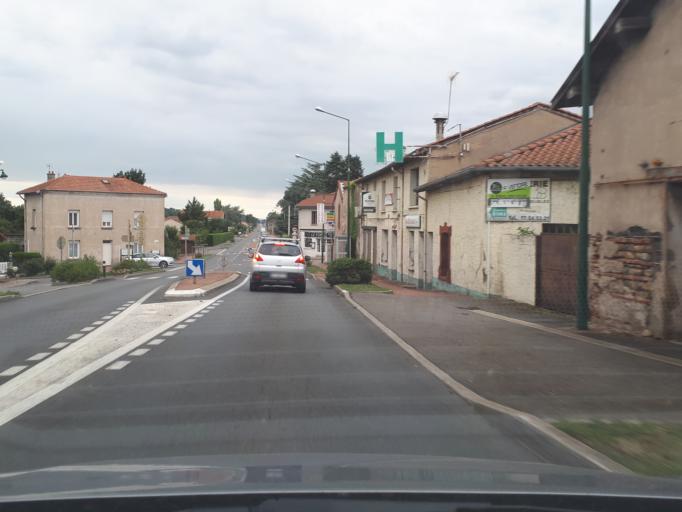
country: FR
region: Rhone-Alpes
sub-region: Departement de la Loire
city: Cuzieu
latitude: 45.6084
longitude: 4.2610
